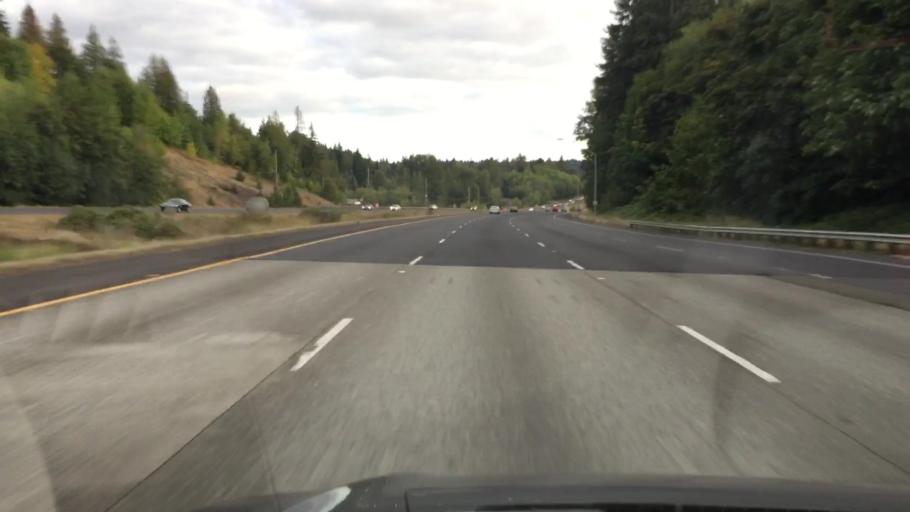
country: US
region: Washington
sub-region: Cowlitz County
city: West Side Highway
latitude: 46.2004
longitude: -122.8927
